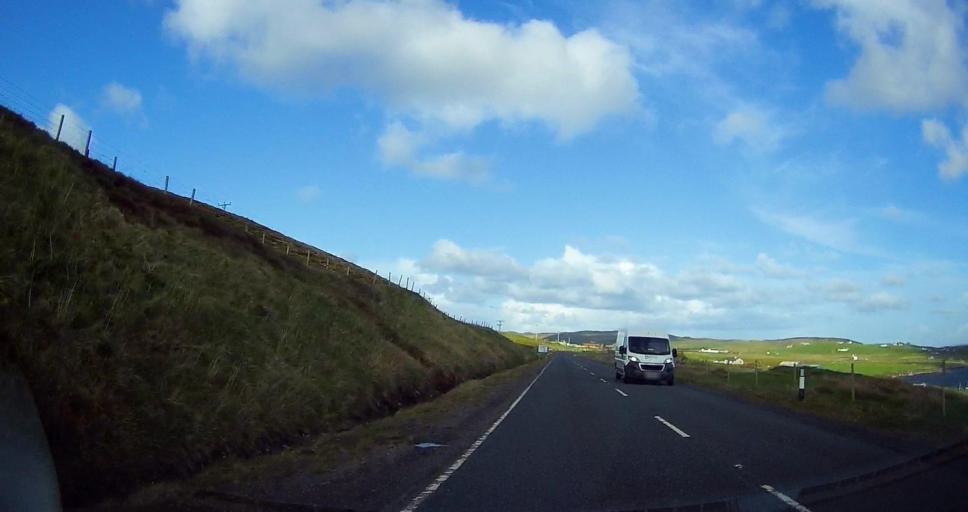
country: GB
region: Scotland
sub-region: Shetland Islands
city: Lerwick
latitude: 60.3529
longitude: -1.1765
